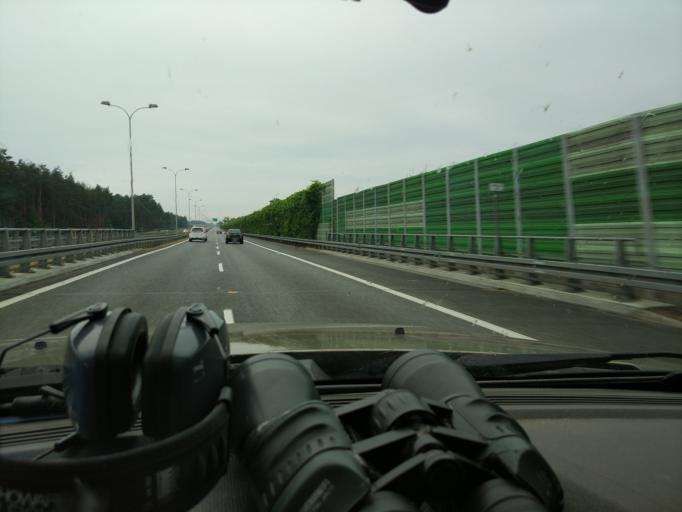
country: PL
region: Masovian Voivodeship
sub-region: Powiat wyszkowski
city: Wyszkow
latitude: 52.5247
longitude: 21.4153
